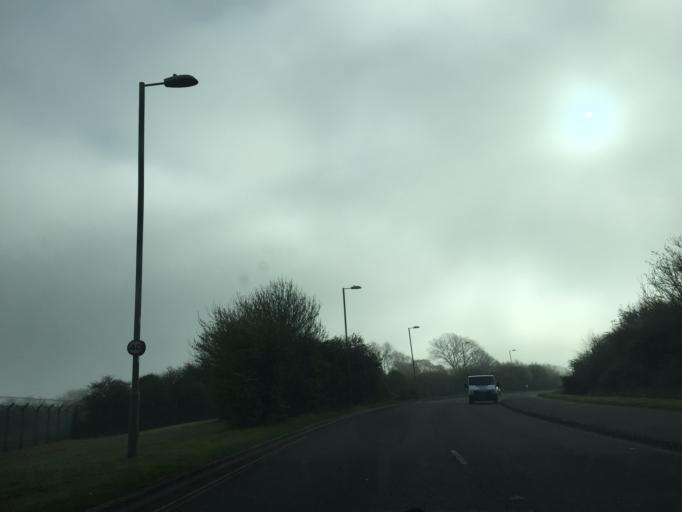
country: GB
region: England
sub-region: Hampshire
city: Gosport
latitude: 50.8183
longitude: -1.1572
